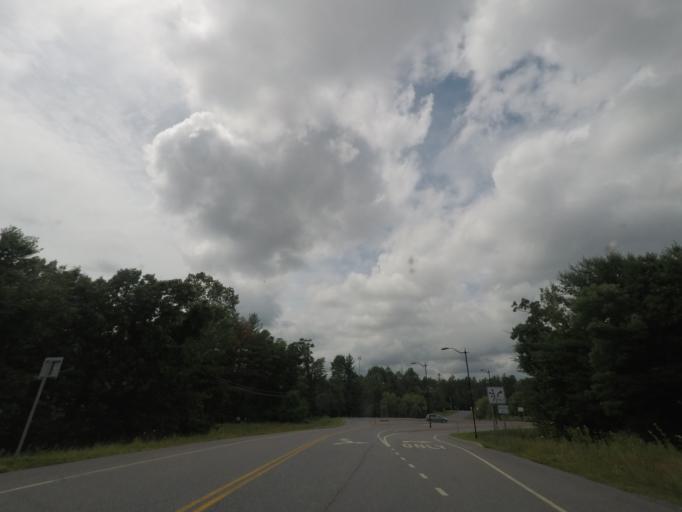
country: US
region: New York
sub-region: Saratoga County
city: Country Knolls
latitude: 42.9651
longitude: -73.7569
